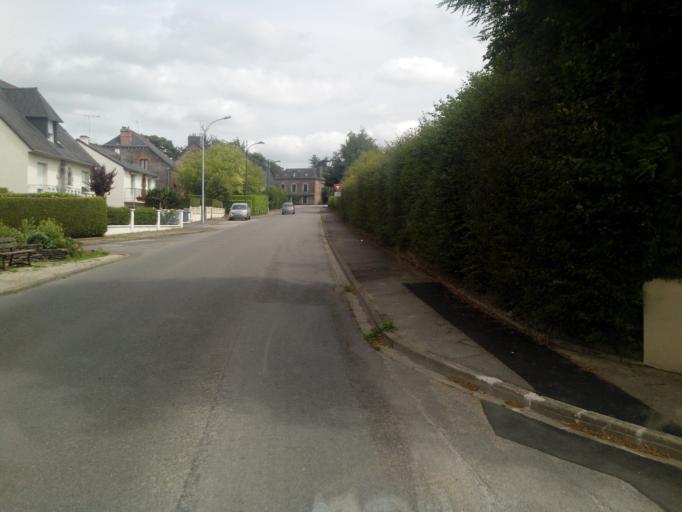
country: FR
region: Brittany
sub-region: Departement d'Ille-et-Vilaine
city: Plelan-le-Grand
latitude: 48.0005
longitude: -2.1071
